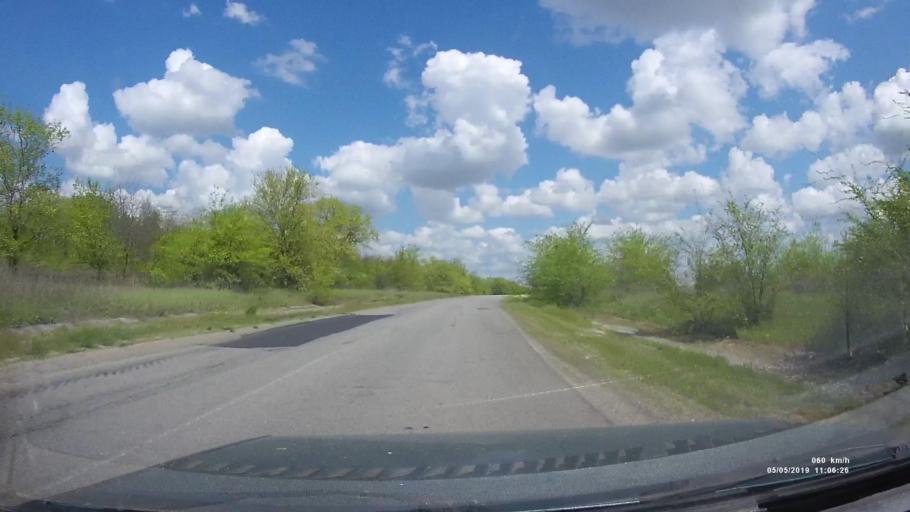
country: RU
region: Rostov
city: Ust'-Donetskiy
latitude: 47.7154
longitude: 40.9109
